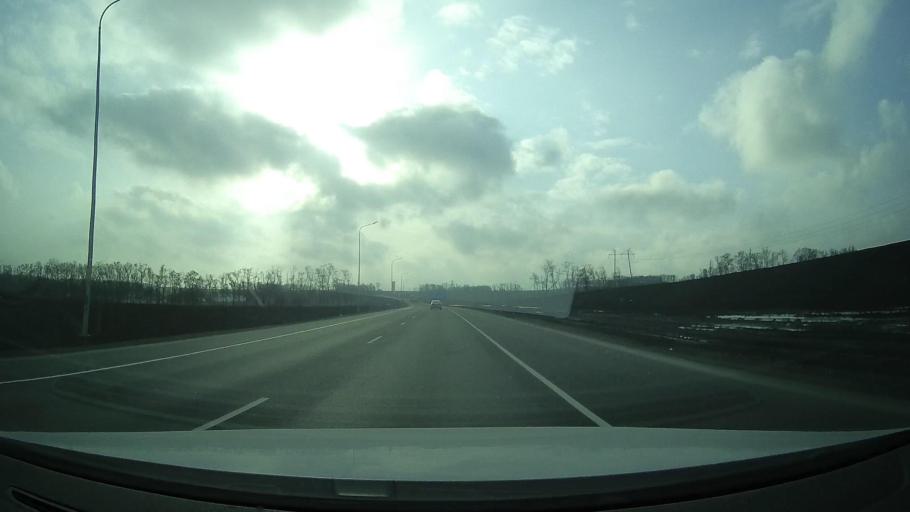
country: RU
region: Rostov
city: Grushevskaya
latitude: 47.3890
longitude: 39.8468
